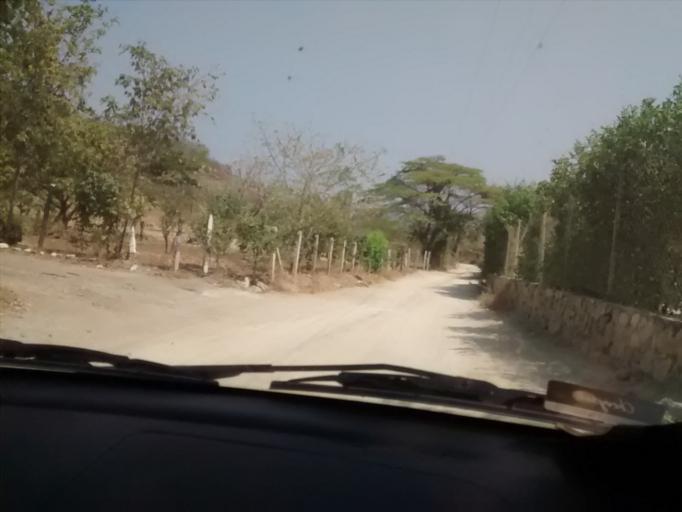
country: CO
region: Magdalena
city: Santa Marta
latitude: 11.1637
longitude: -74.2181
